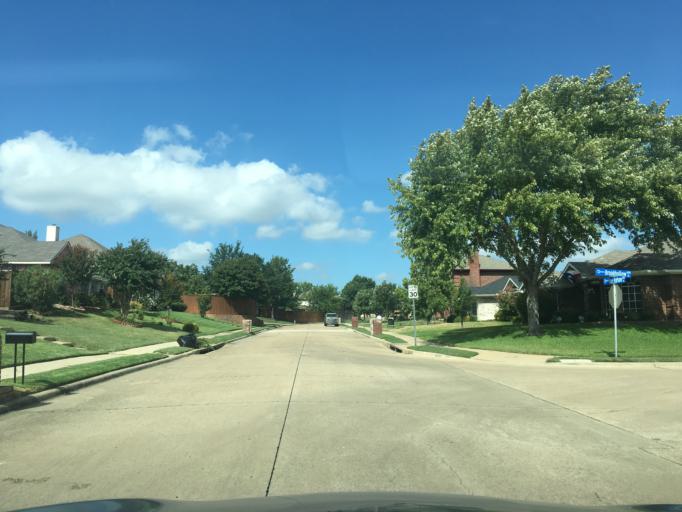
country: US
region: Texas
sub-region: Dallas County
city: Sachse
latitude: 32.9699
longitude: -96.5949
